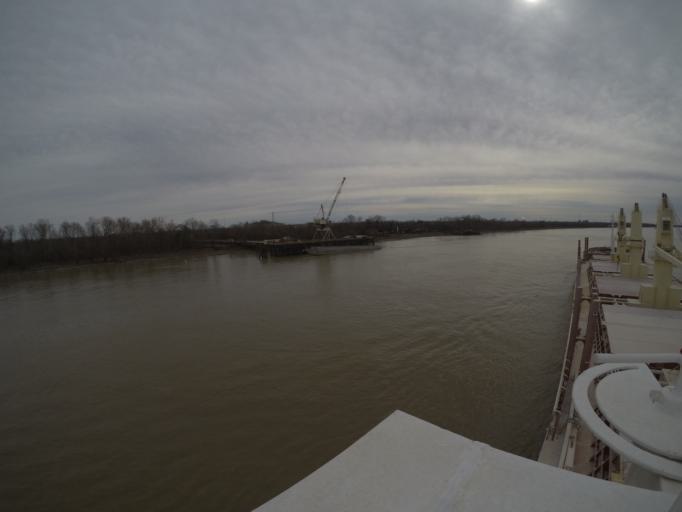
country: US
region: Louisiana
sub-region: Saint John the Baptist Parish
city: Laplace
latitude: 30.0395
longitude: -90.4731
